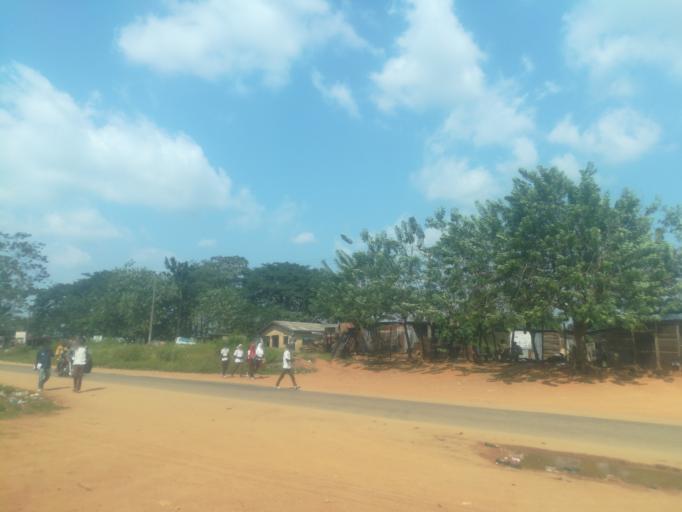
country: NG
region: Oyo
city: Moniya
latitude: 7.5407
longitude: 3.9111
